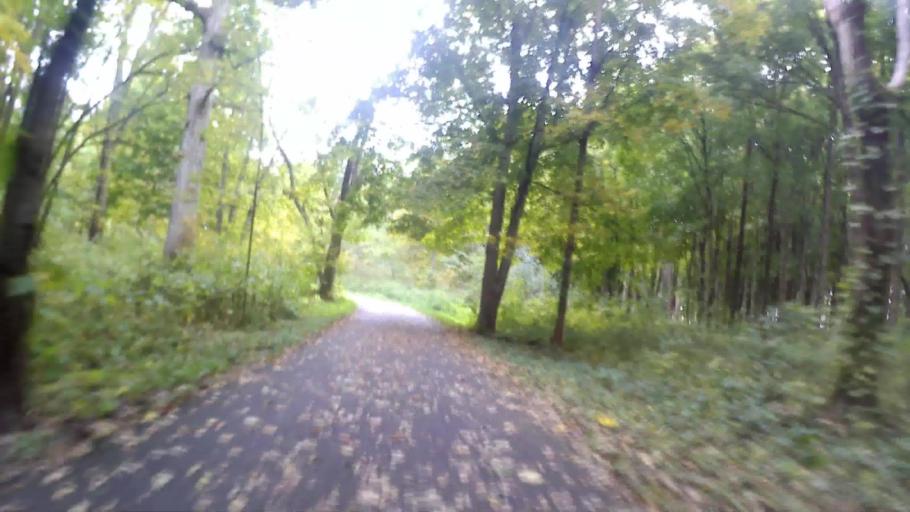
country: US
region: Illinois
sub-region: Kane County
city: Sugar Grove
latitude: 41.7861
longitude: -88.4435
